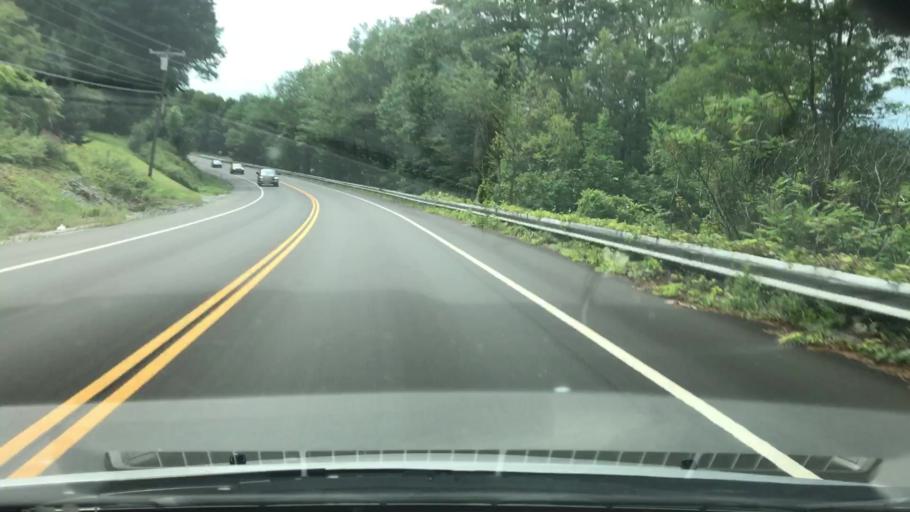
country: US
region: New Hampshire
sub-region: Grafton County
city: Hanover
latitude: 43.7479
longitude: -72.2287
